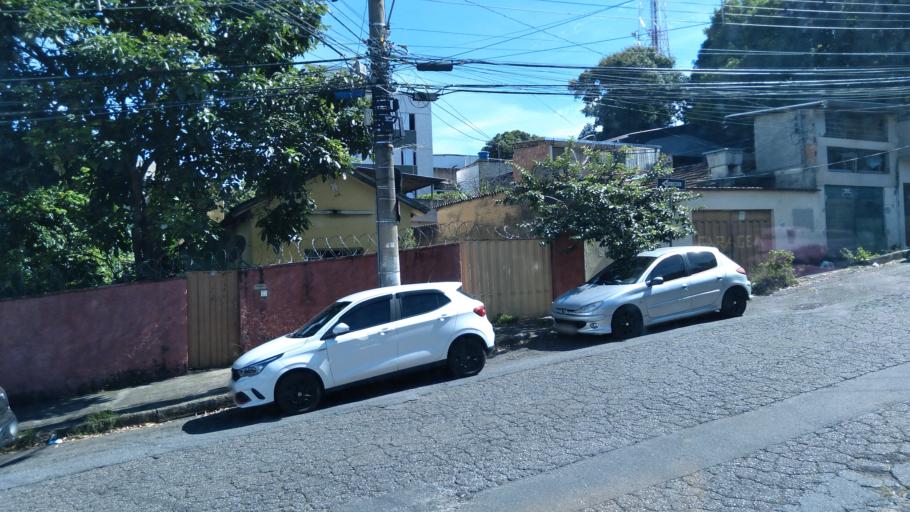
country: BR
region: Minas Gerais
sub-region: Contagem
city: Contagem
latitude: -19.8996
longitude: -44.0065
